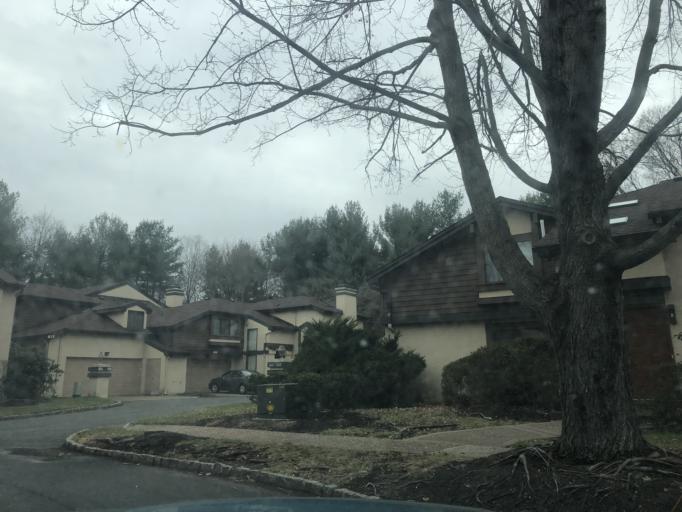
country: US
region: New Jersey
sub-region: Somerset County
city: Kingston
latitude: 40.3483
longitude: -74.6199
